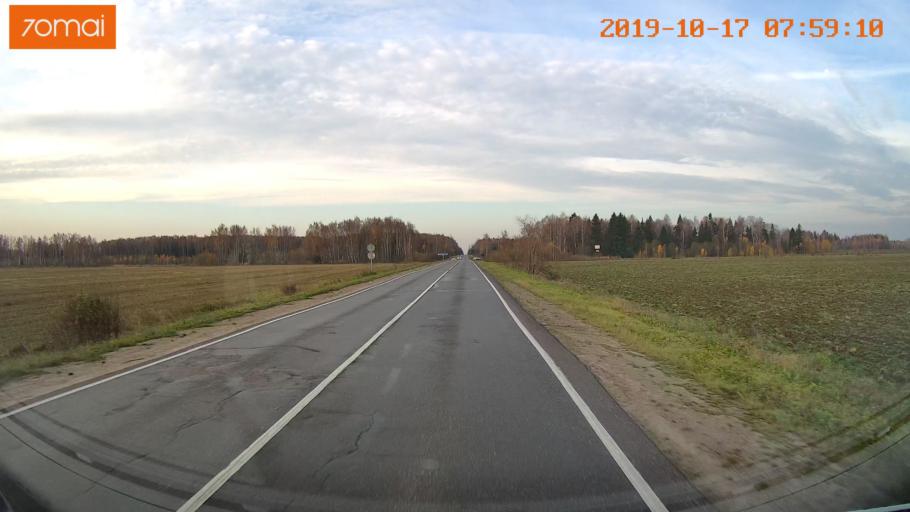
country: RU
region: Vladimir
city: Bavleny
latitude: 56.3959
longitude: 39.5436
